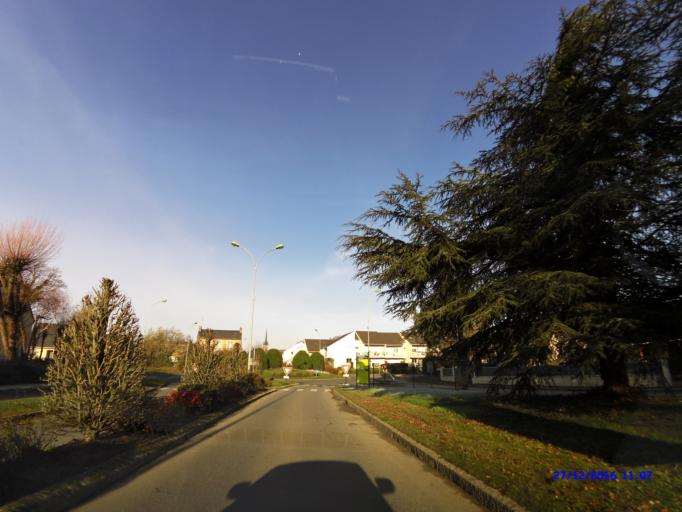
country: FR
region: Brittany
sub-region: Departement d'Ille-et-Vilaine
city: Saint-Erblon
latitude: 48.0169
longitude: -1.6484
